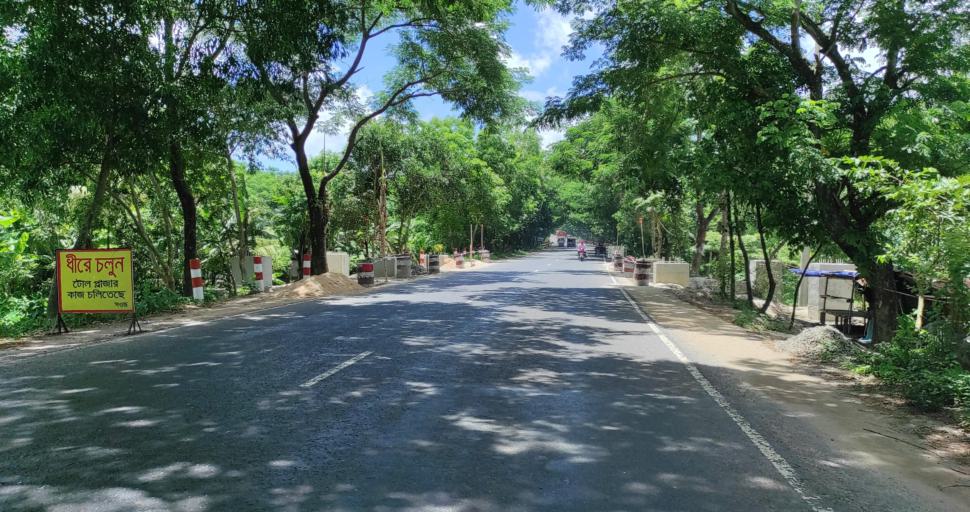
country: BD
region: Barisal
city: Gaurnadi
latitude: 22.8287
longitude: 90.2588
